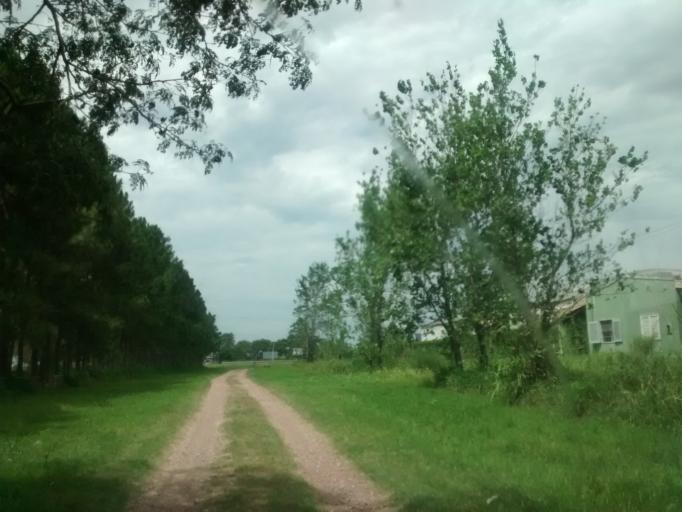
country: AR
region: Chaco
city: Resistencia
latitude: -27.4139
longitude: -58.9741
